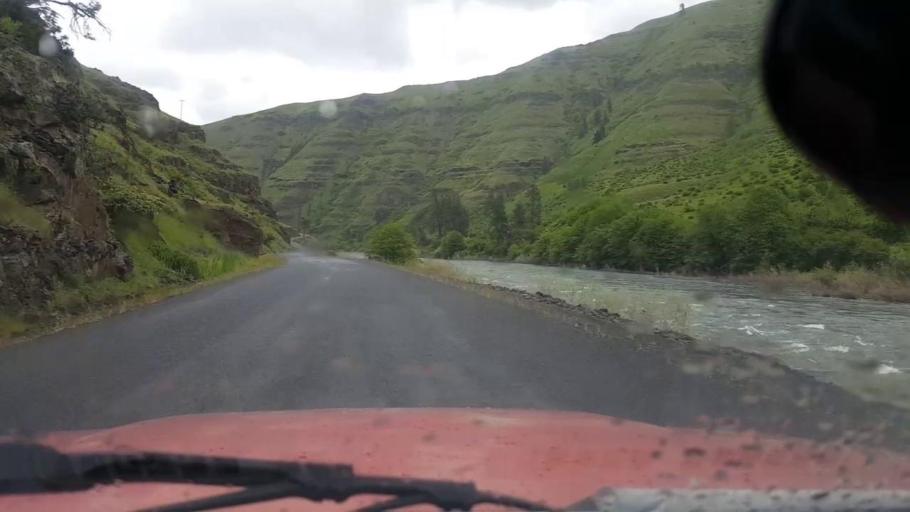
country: US
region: Washington
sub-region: Asotin County
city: Asotin
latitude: 46.0302
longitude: -117.3032
